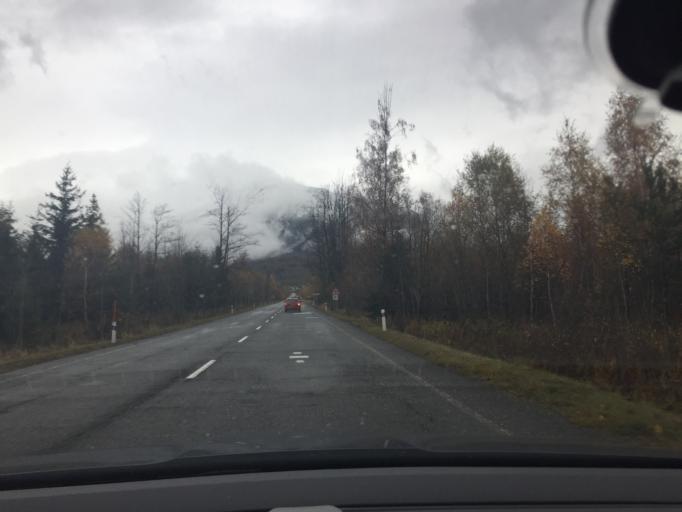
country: SK
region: Presovsky
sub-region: Okres Poprad
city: Vysoke Tatry
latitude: 49.1284
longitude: 20.2401
